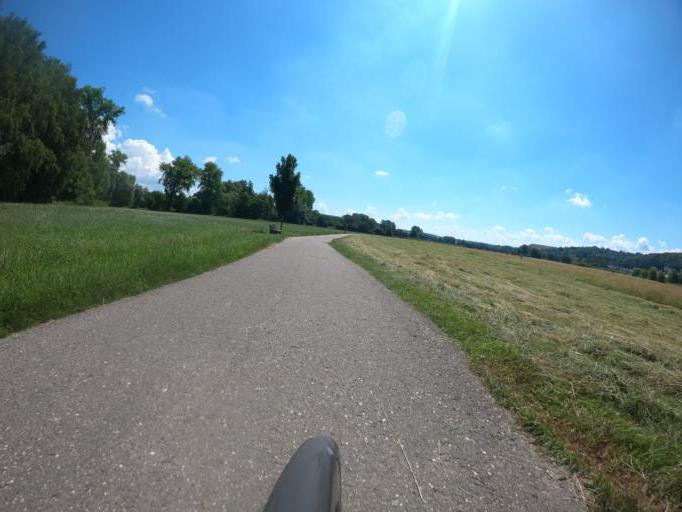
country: DE
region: Baden-Wuerttemberg
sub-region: Karlsruhe Region
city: Bammental
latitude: 49.3437
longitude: 8.7847
